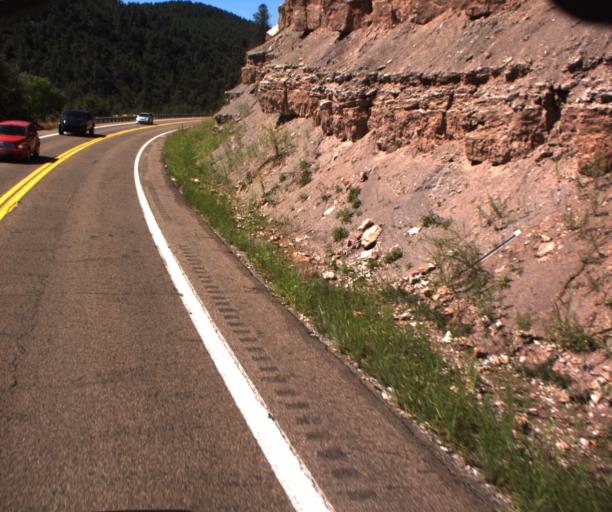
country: US
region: Arizona
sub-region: Navajo County
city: Cibecue
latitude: 33.8443
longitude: -110.4254
